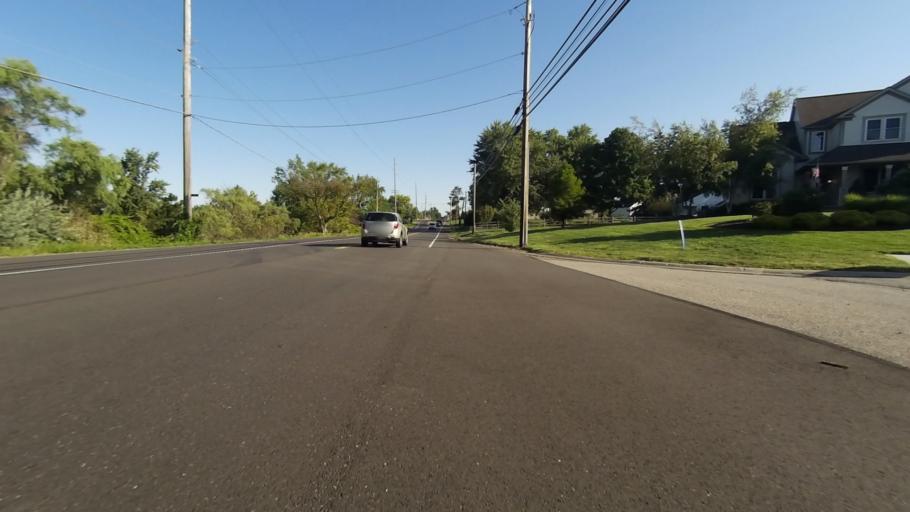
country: US
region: Ohio
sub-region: Portage County
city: Aurora
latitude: 41.2980
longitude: -81.3456
